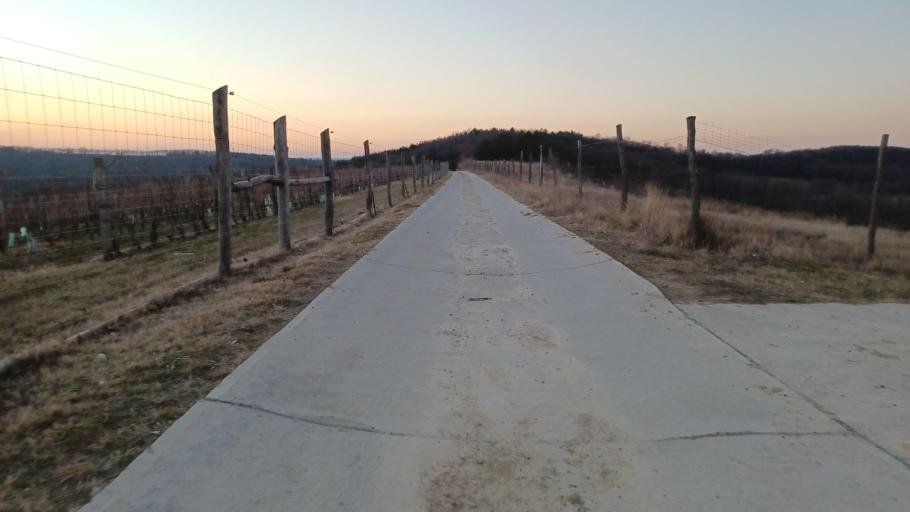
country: HU
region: Tolna
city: Szentgalpuszta
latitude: 46.3452
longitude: 18.6367
